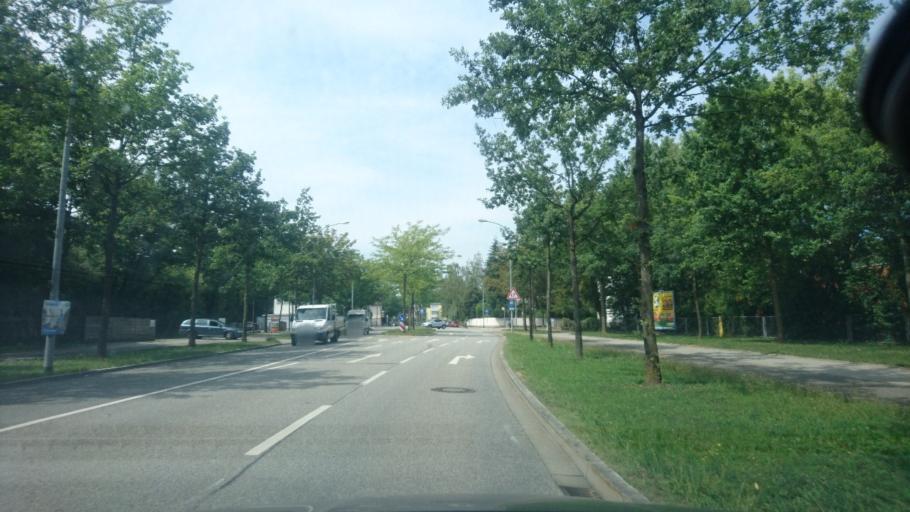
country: DE
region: Bavaria
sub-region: Upper Palatinate
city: Sinzing
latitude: 49.0128
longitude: 12.0477
